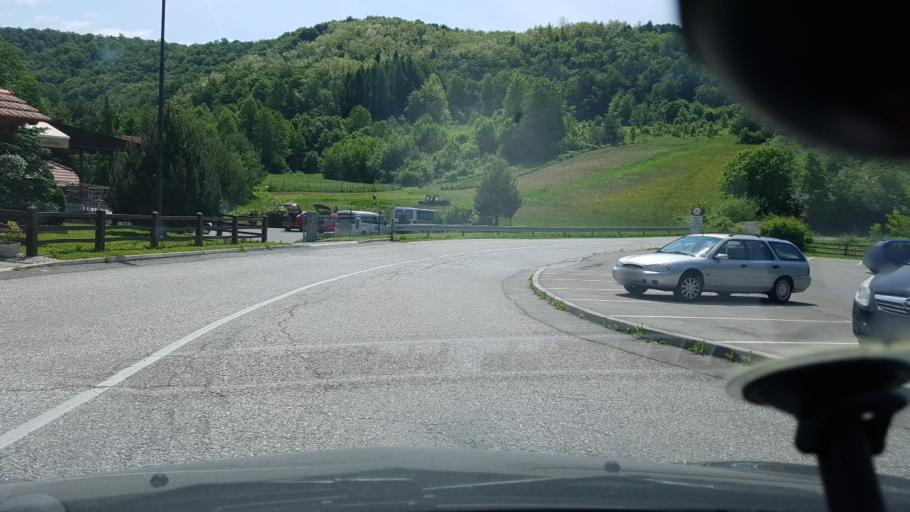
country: HR
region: Krapinsko-Zagorska
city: Marija Bistrica
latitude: 45.9845
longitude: 16.1145
